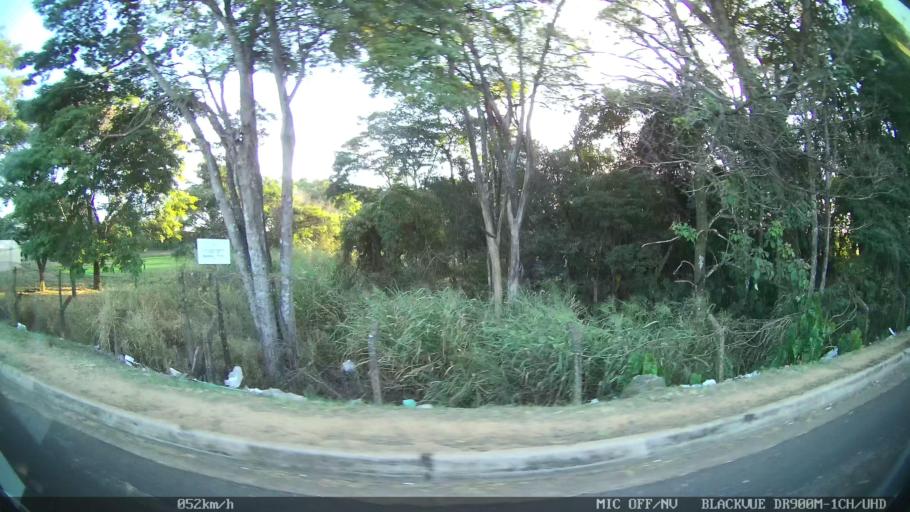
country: BR
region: Sao Paulo
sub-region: Franca
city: Franca
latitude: -20.4974
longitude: -47.4072
